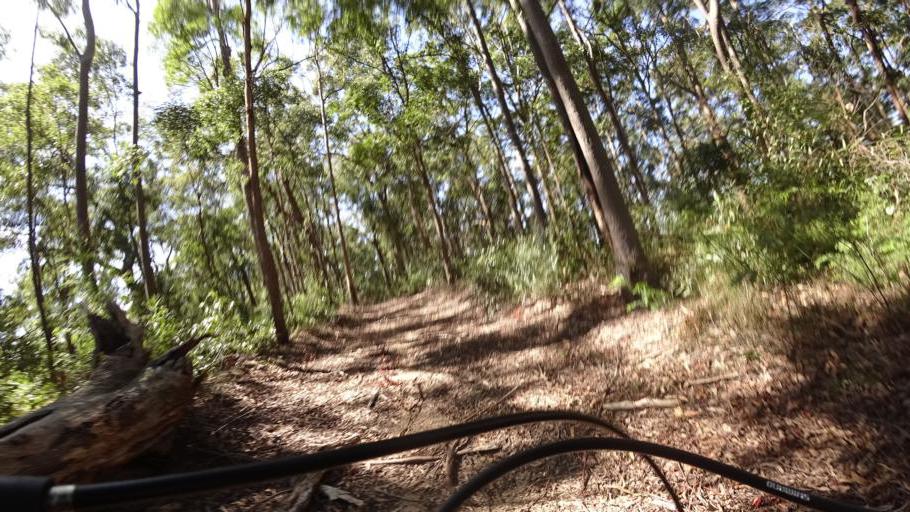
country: AU
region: Queensland
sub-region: Moreton Bay
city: Highvale
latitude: -27.4117
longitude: 152.7819
